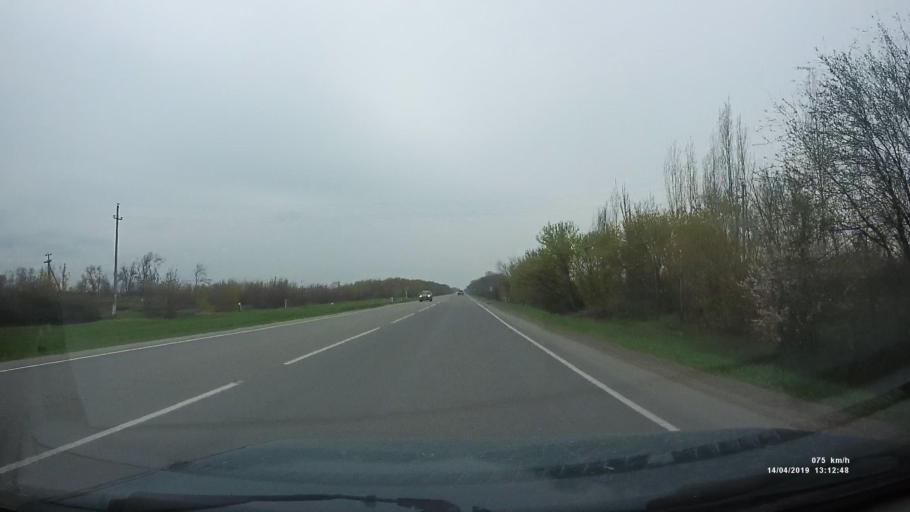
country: RU
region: Rostov
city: Kuleshovka
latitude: 47.1010
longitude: 39.6327
